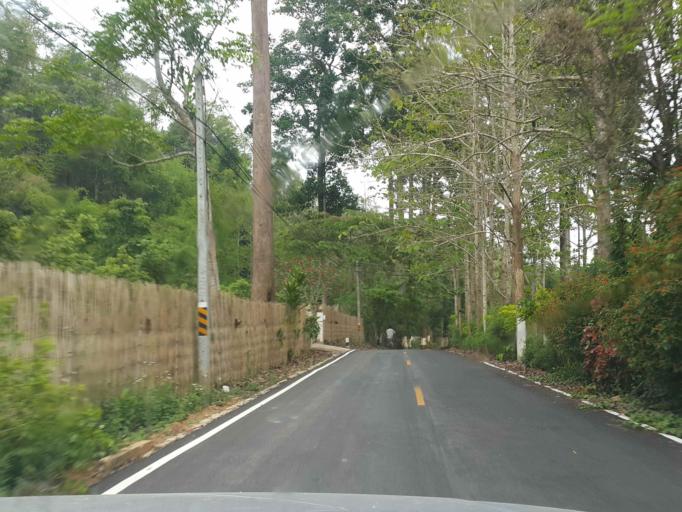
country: TH
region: Chiang Mai
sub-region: Amphoe Chiang Dao
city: Chiang Dao
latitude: 19.4054
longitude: 98.9271
